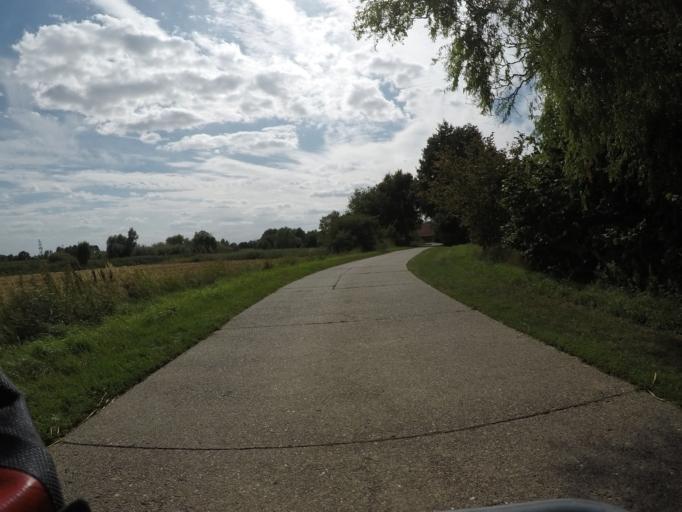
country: DE
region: Lower Saxony
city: Handorf
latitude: 53.3639
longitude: 10.3136
